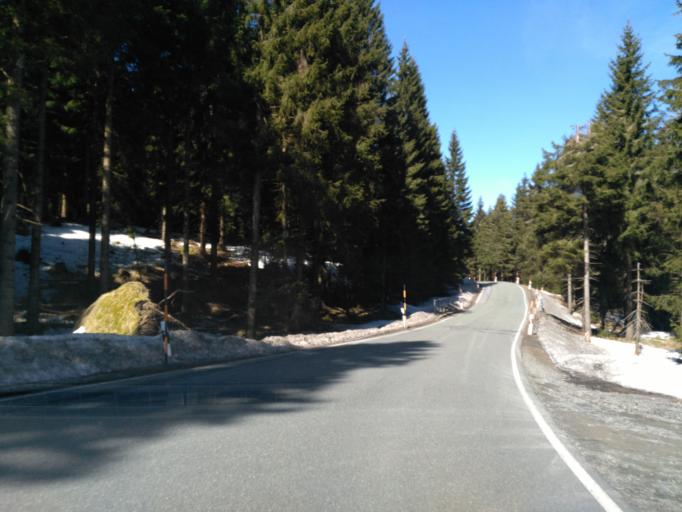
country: DE
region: Saxony
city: Kurort Oberwiesenthal
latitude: 50.4317
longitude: 12.9029
